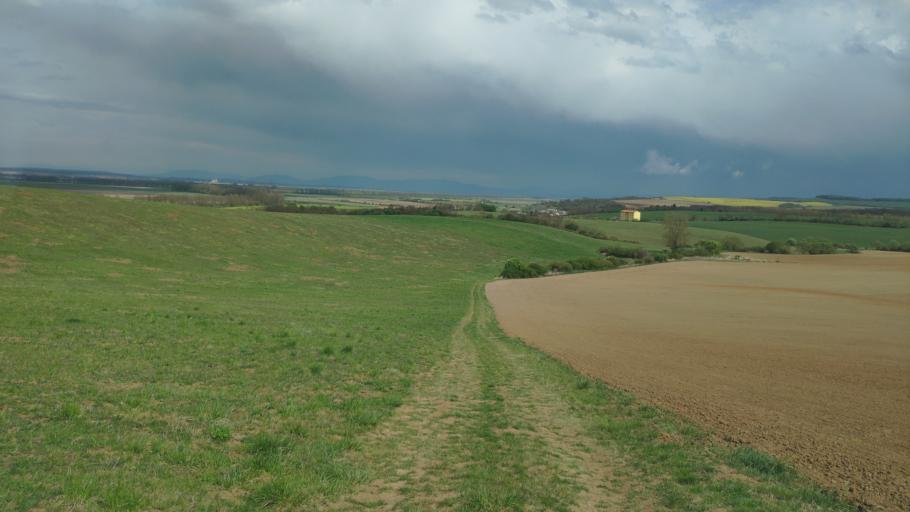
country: SK
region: Kosicky
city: Moldava nad Bodvou
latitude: 48.5564
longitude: 20.9467
